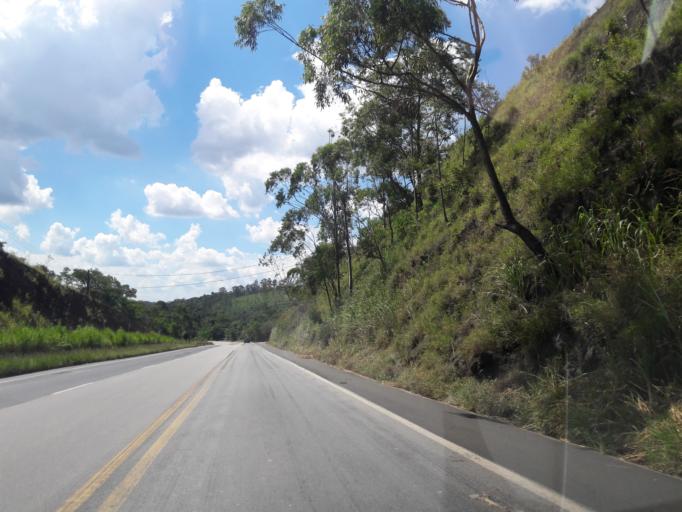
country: BR
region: Sao Paulo
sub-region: Campo Limpo Paulista
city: Campo Limpo Paulista
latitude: -23.2498
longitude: -46.7902
